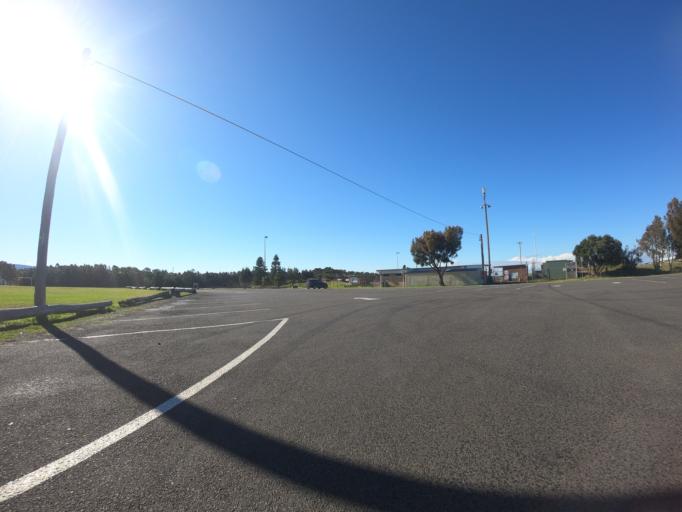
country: AU
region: New South Wales
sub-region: Wollongong
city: East Corrimal
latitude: -34.3839
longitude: 150.9105
